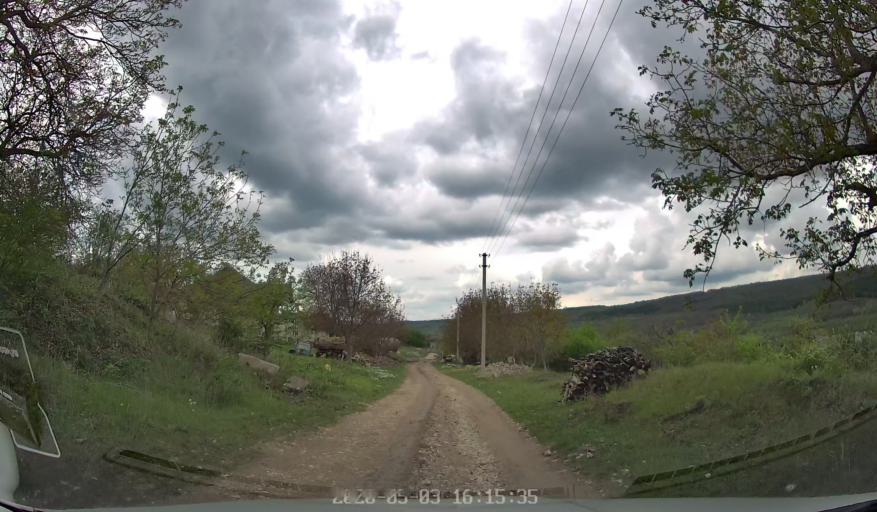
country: MD
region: Calarasi
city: Calarasi
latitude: 47.1984
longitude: 28.3479
